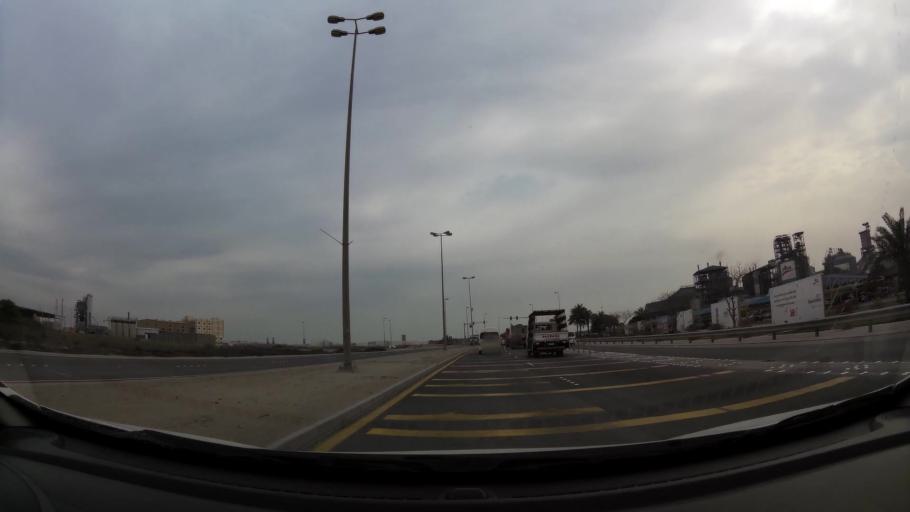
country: BH
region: Northern
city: Sitrah
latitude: 26.0960
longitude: 50.6080
